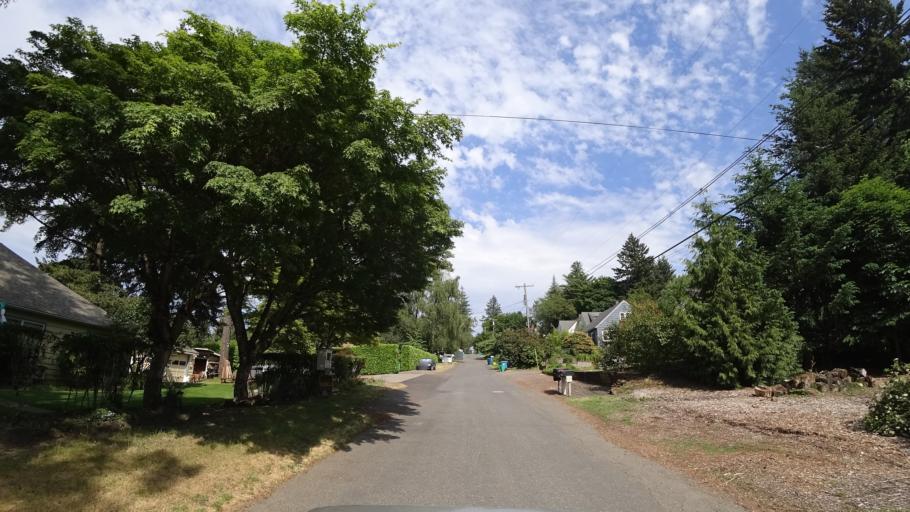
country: US
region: Oregon
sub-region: Washington County
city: Garden Home-Whitford
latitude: 45.4561
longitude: -122.7402
